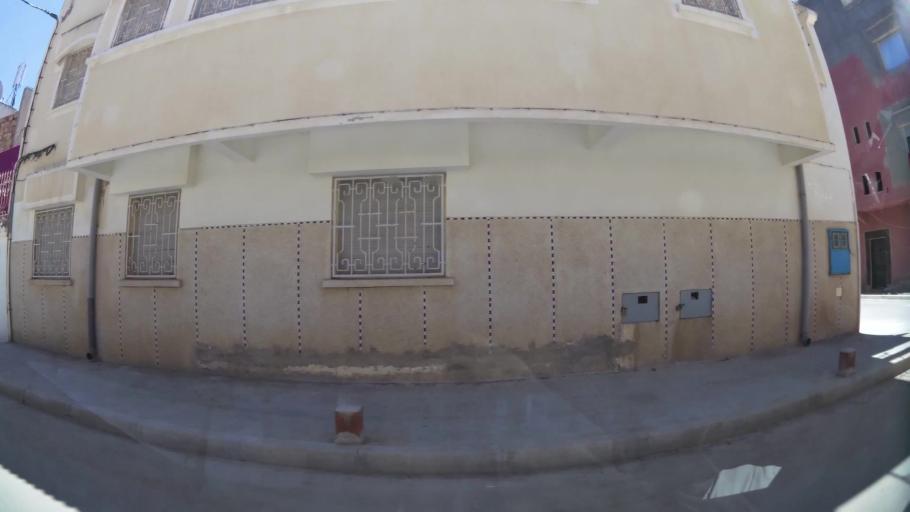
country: MA
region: Oriental
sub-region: Berkane-Taourirt
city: Madagh
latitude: 35.0796
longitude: -2.2184
